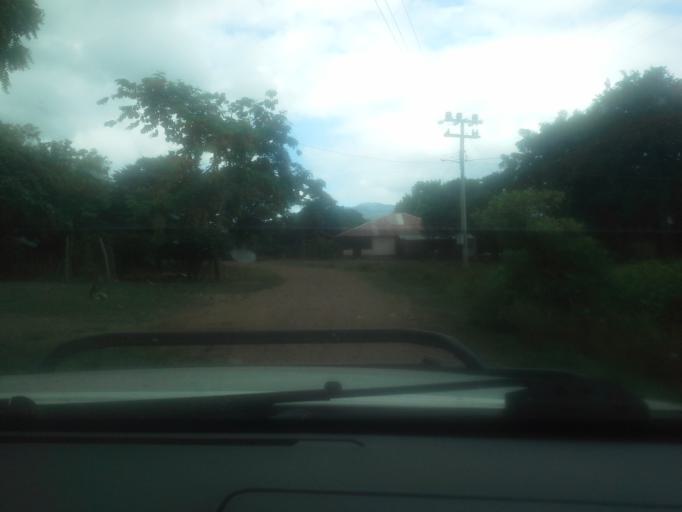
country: NI
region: Matagalpa
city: Ciudad Dario
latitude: 12.8232
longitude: -86.1909
